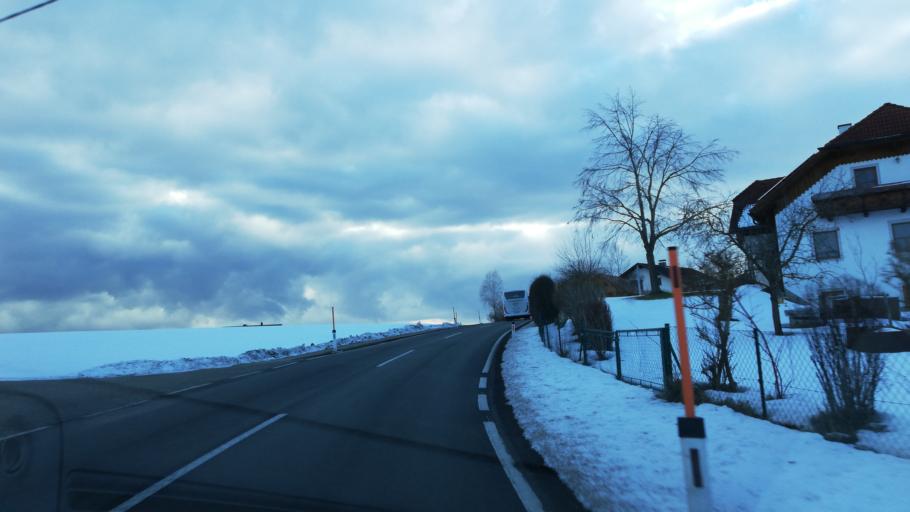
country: AT
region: Upper Austria
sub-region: Politischer Bezirk Urfahr-Umgebung
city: Herzogsdorf
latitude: 48.4191
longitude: 14.0959
